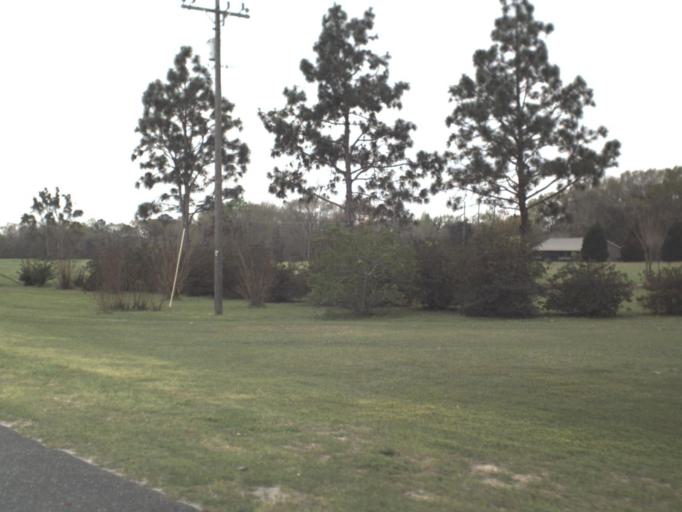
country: US
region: Florida
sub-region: Calhoun County
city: Blountstown
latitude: 30.4592
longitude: -85.1914
